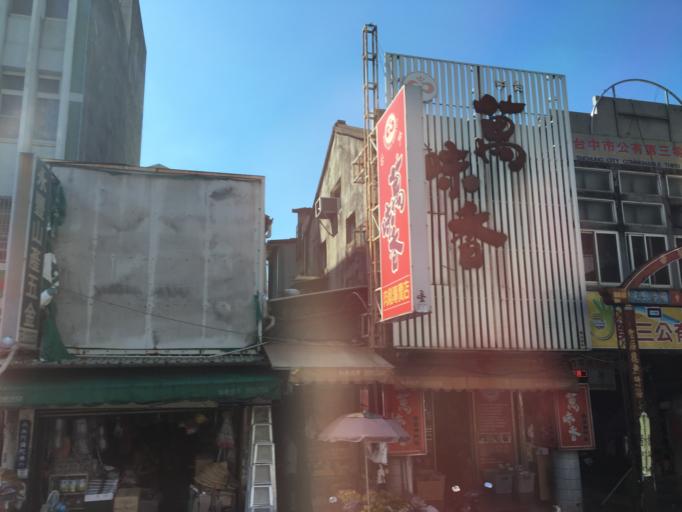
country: TW
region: Taiwan
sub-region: Taichung City
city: Taichung
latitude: 24.1335
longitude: 120.6833
